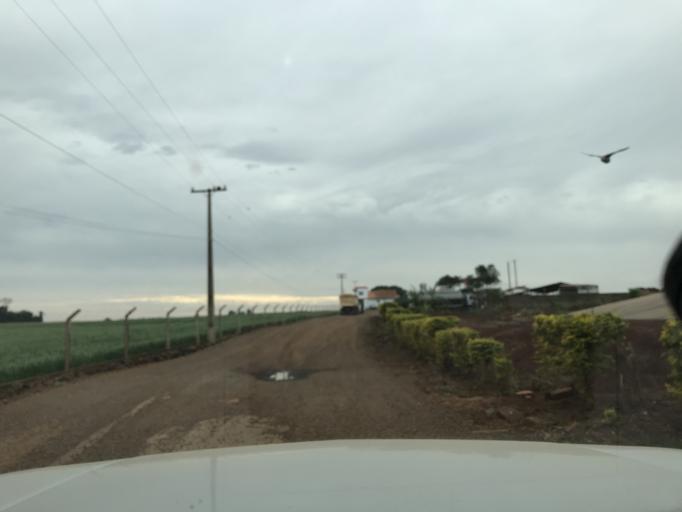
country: BR
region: Parana
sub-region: Marechal Candido Rondon
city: Marechal Candido Rondon
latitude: -24.4601
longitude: -53.9666
